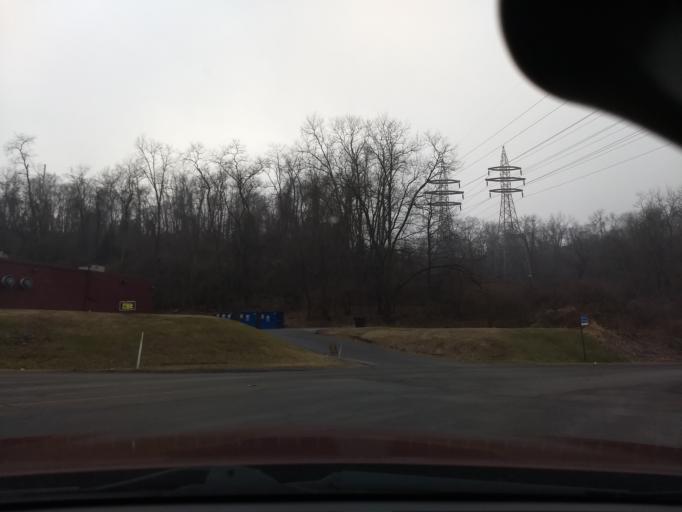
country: US
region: Pennsylvania
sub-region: Allegheny County
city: East Pittsburgh
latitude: 40.3833
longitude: -79.8279
